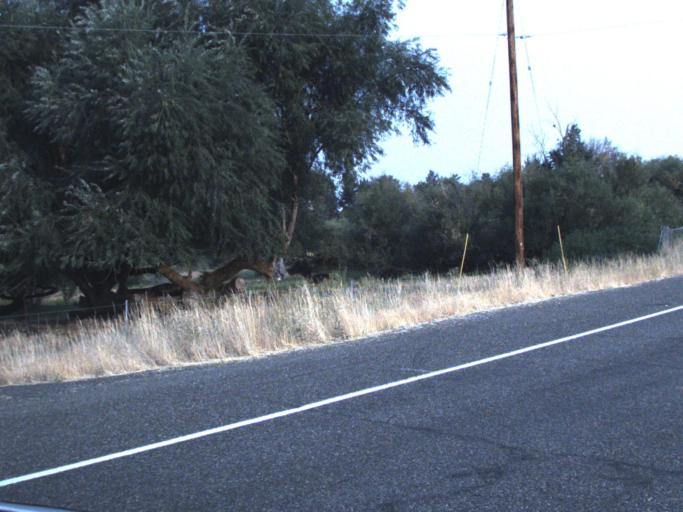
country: US
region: Washington
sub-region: Kittitas County
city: Ellensburg
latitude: 47.0431
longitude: -120.6086
